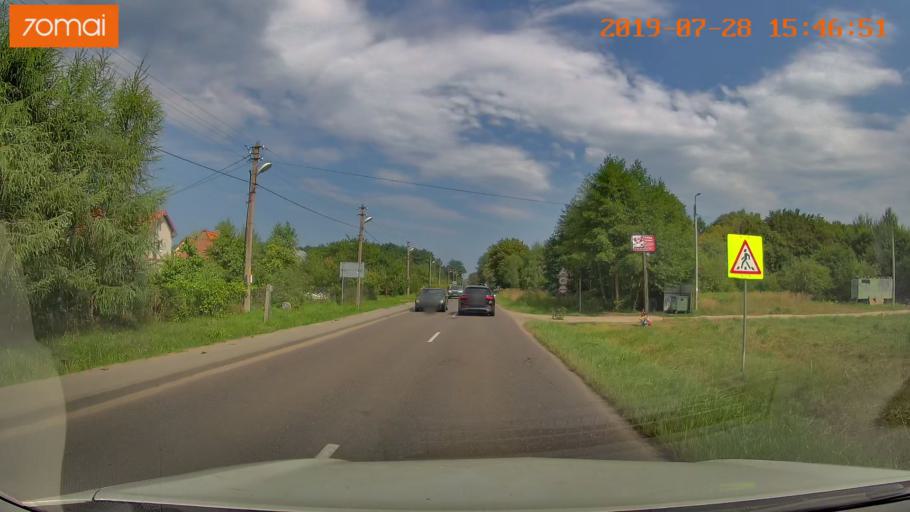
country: RU
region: Kaliningrad
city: Otradnoye
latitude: 54.9430
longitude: 20.0591
